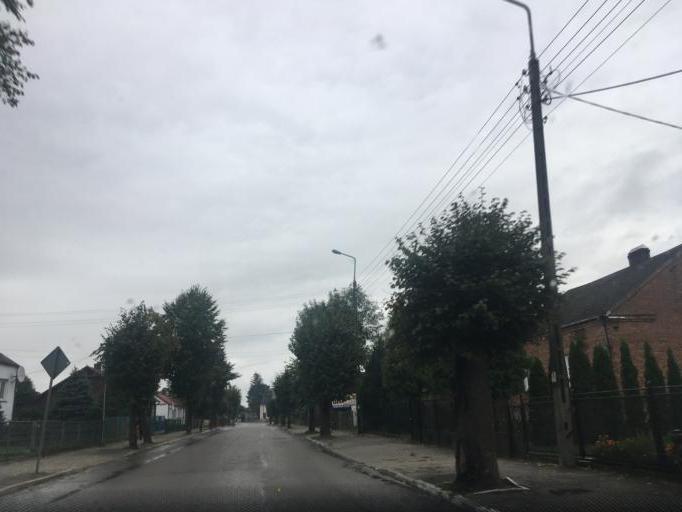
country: PL
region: Podlasie
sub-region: Powiat bielski
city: Bransk
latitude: 52.7437
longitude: 22.8445
